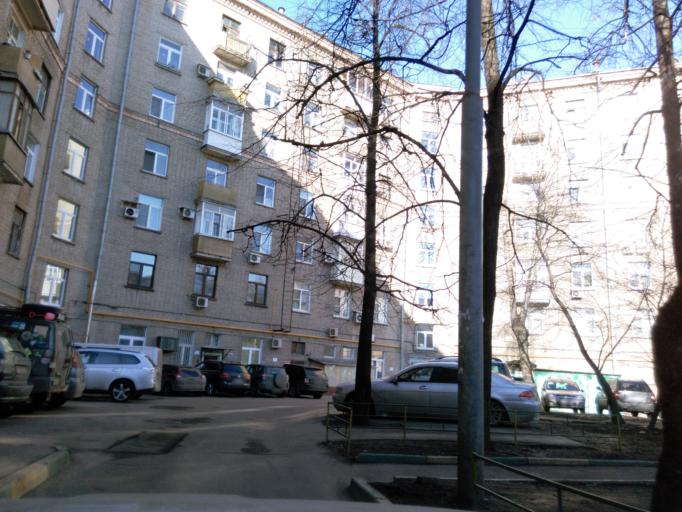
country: RU
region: Moskovskaya
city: Koptevo
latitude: 55.8166
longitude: 37.5229
